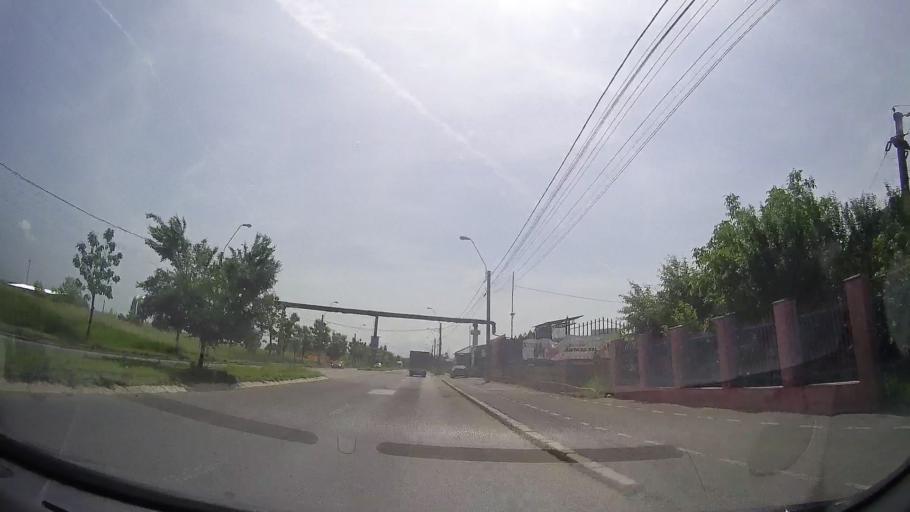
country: RO
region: Hunedoara
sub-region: Municipiul Deva
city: Deva
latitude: 45.8953
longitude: 22.8983
